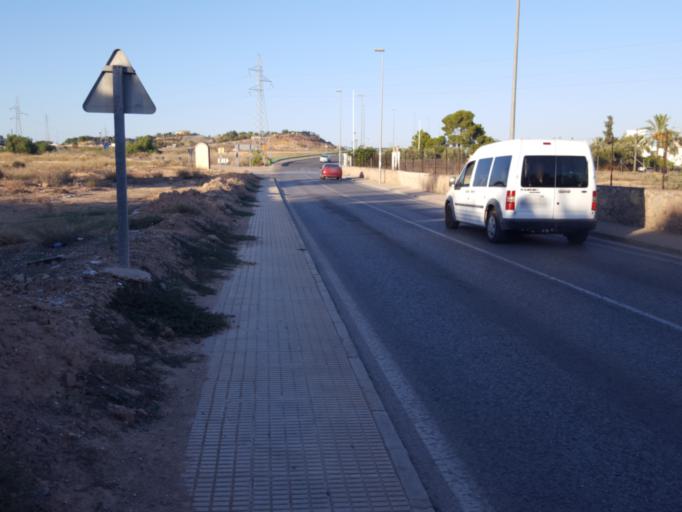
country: ES
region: Murcia
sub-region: Murcia
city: Murcia
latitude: 38.0023
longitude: -1.1677
